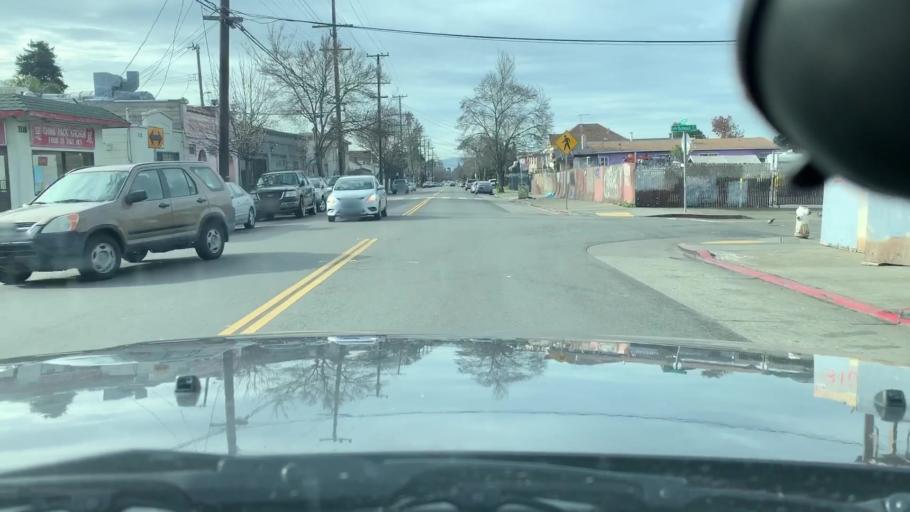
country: US
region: California
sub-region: Alameda County
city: Piedmont
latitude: 37.7910
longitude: -122.2053
